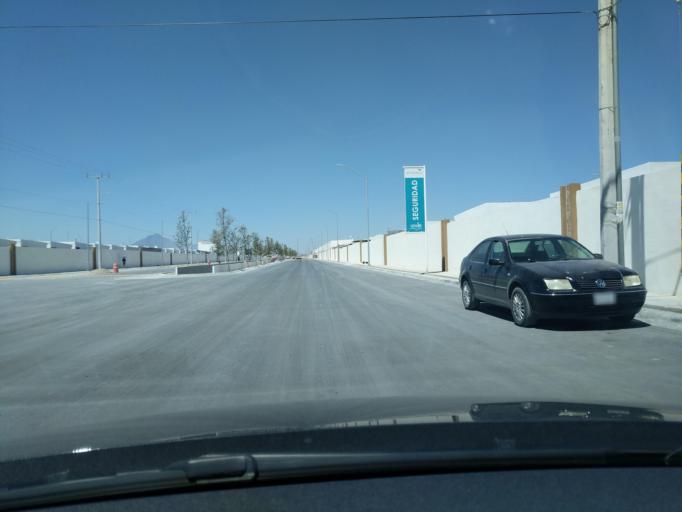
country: MX
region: Nuevo Leon
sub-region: Apodaca
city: Artemio Trevino
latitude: 25.8417
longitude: -100.1377
